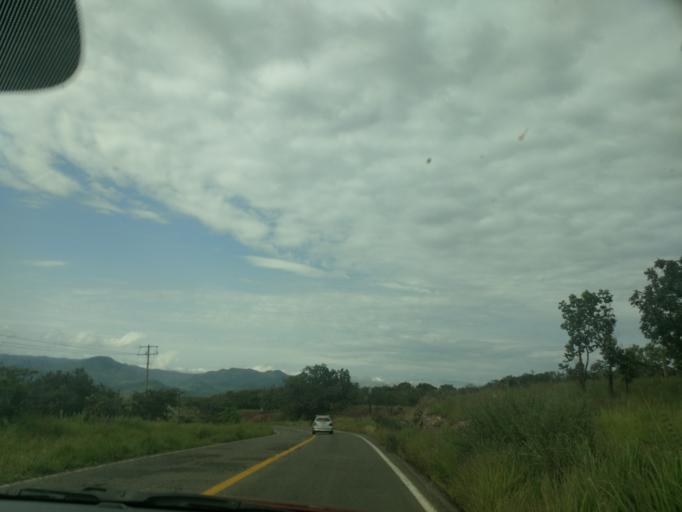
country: MX
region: Jalisco
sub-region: Atengo
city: Soyatlan del Oro
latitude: 20.5484
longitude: -104.3043
